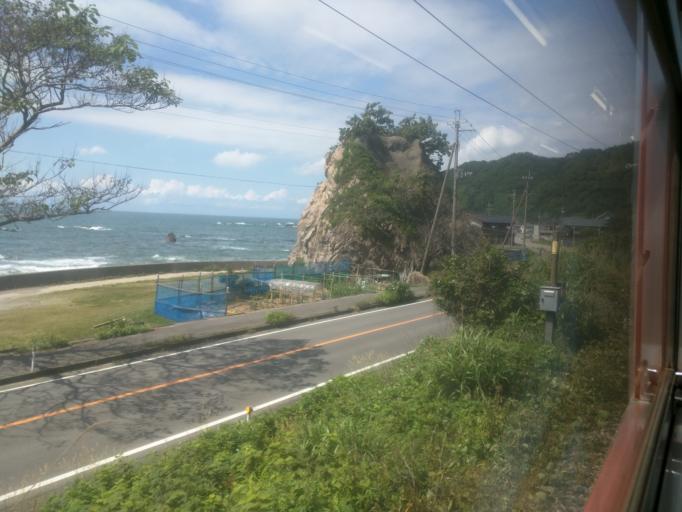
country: JP
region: Niigata
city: Murakami
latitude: 38.4298
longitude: 139.4807
